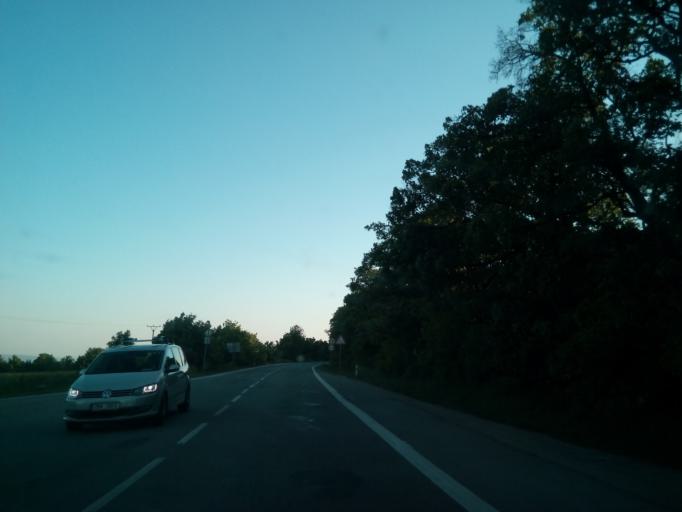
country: CZ
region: South Moravian
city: Bilovice nad Svitavou
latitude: 49.2303
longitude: 16.7012
